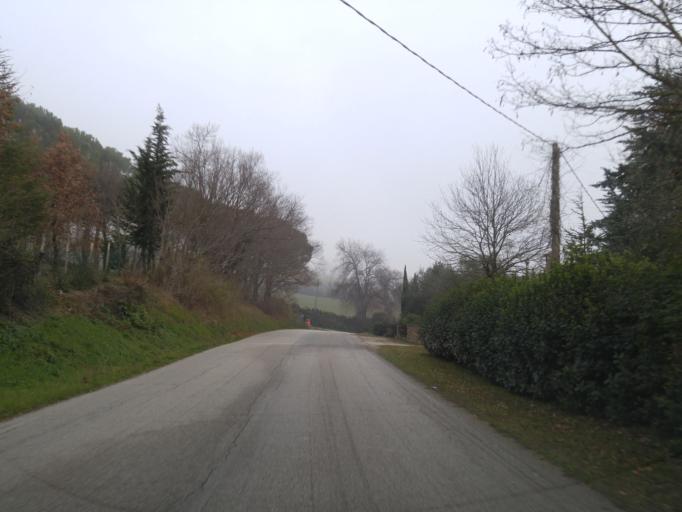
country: IT
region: The Marches
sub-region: Provincia di Pesaro e Urbino
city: Isola del Piano
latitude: 43.7373
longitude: 12.7934
